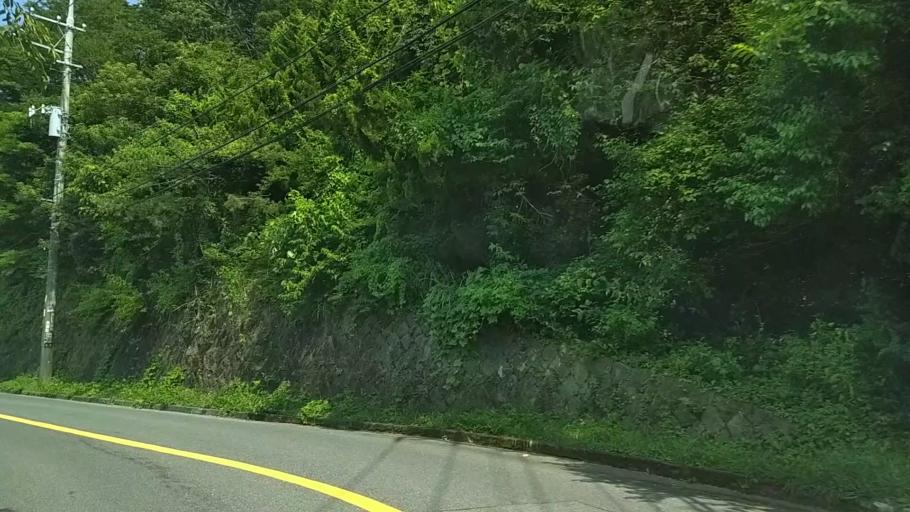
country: JP
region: Shizuoka
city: Ito
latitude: 34.9273
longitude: 139.1068
